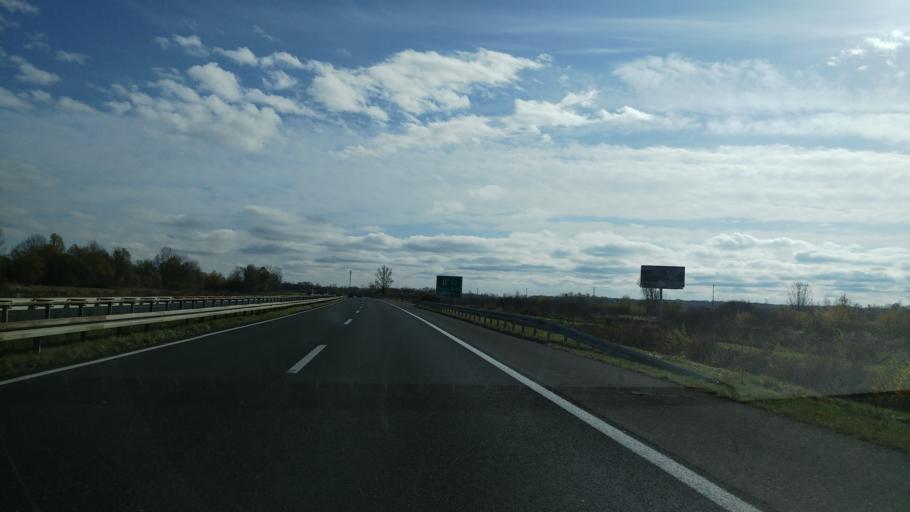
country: HR
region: Zagrebacka
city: Lupoglav
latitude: 45.6985
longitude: 16.3626
